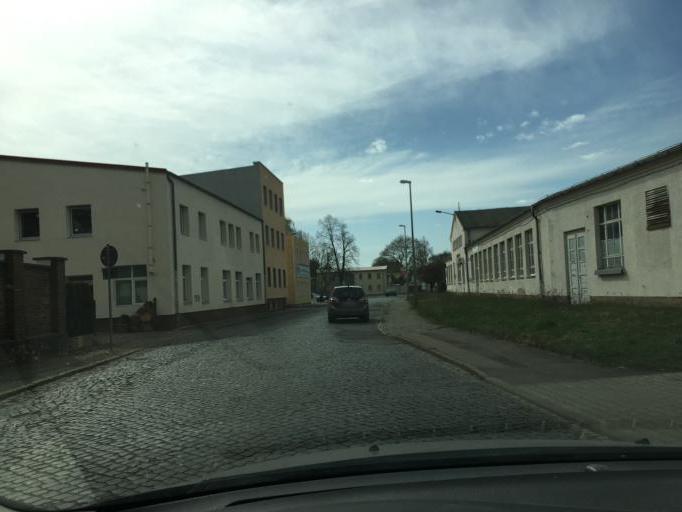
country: DE
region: Saxony
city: Taucha
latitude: 51.3495
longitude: 12.4938
